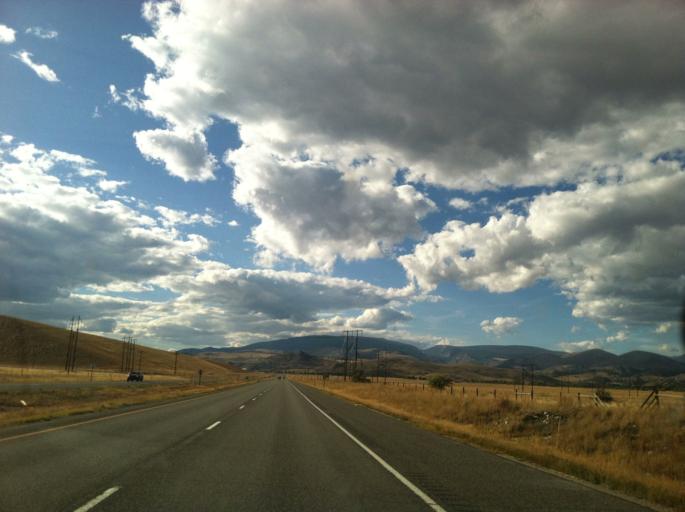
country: US
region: Montana
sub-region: Deer Lodge County
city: Anaconda
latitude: 46.1174
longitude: -112.8716
